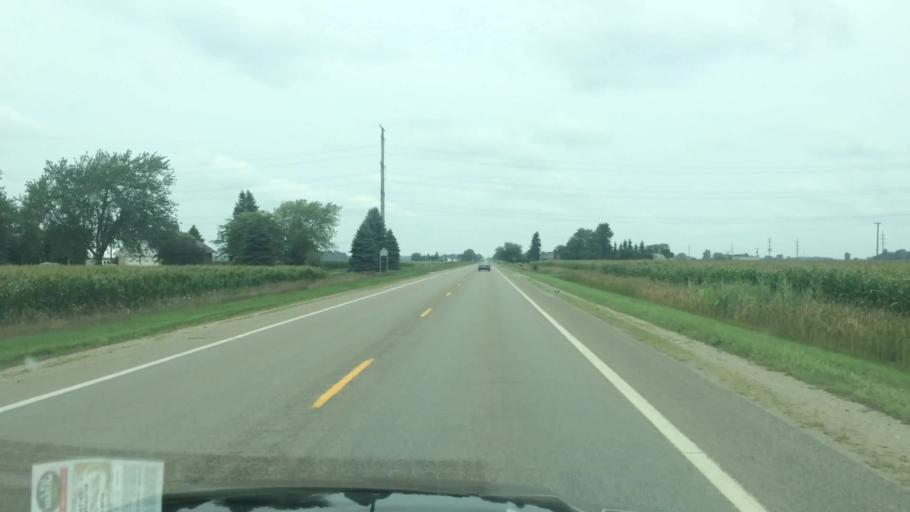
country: US
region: Michigan
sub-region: Huron County
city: Bad Axe
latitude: 43.8391
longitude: -83.0015
